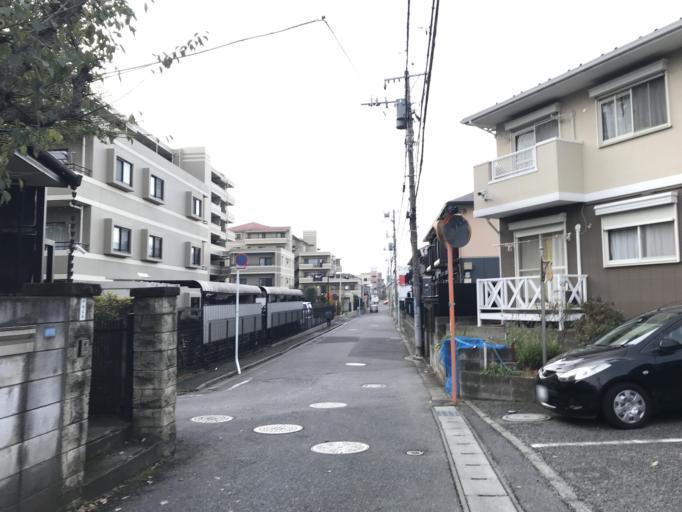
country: JP
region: Chiba
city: Funabashi
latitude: 35.7618
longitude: 140.0015
